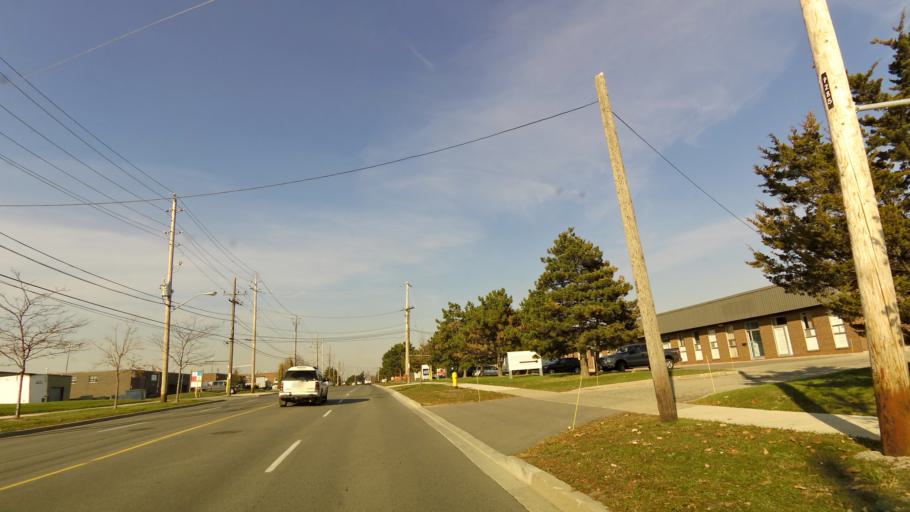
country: CA
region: Ontario
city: Concord
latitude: 43.7678
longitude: -79.5312
